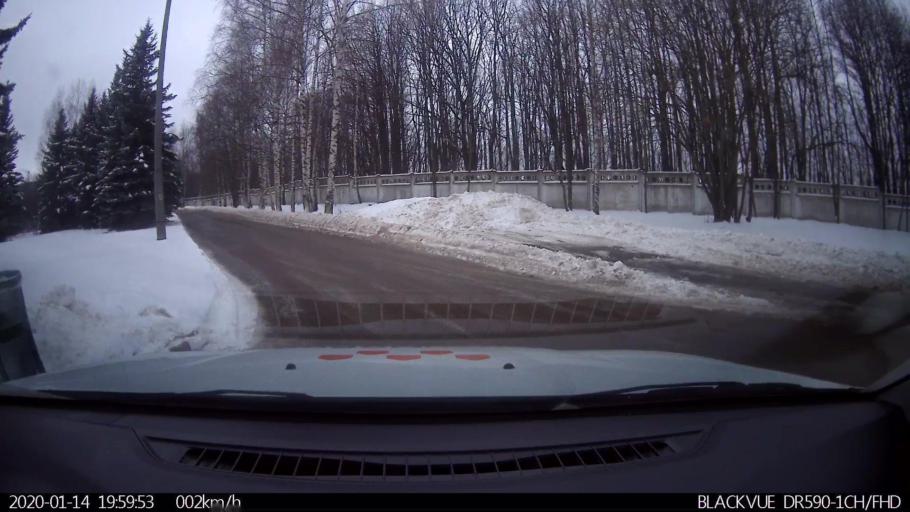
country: RU
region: Nizjnij Novgorod
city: Nizhniy Novgorod
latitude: 56.2405
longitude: 43.9440
